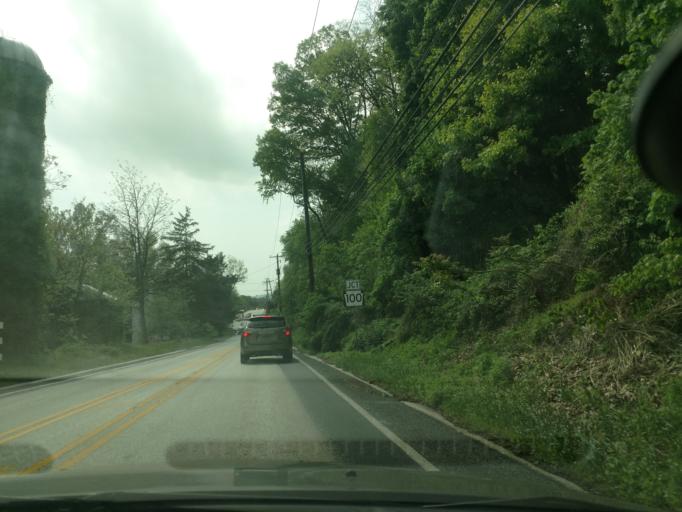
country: US
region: Pennsylvania
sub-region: Chester County
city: Kenilworth
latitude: 40.1751
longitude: -75.6603
